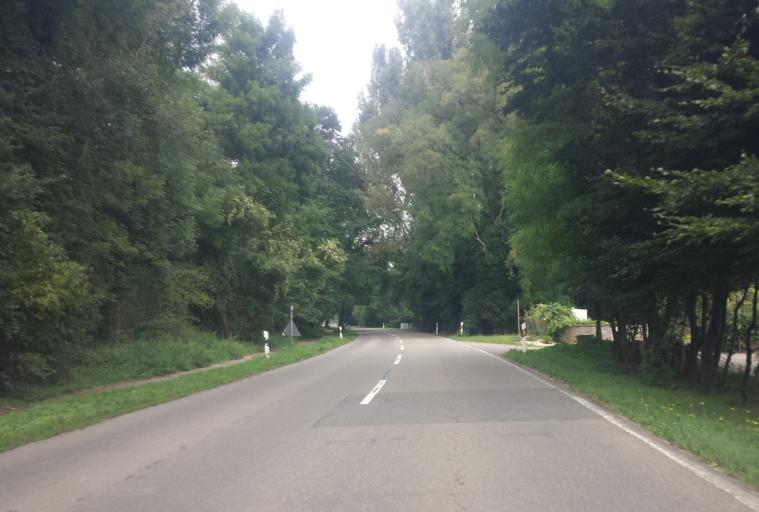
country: DE
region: Rheinland-Pfalz
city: Schifferstadt
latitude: 49.4092
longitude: 8.3645
